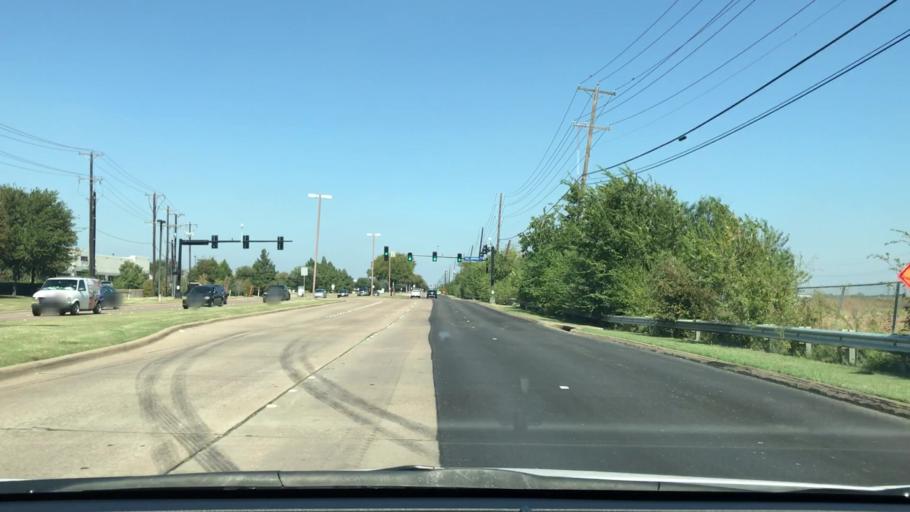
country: US
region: Texas
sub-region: Dallas County
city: Coppell
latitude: 32.9344
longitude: -96.9935
